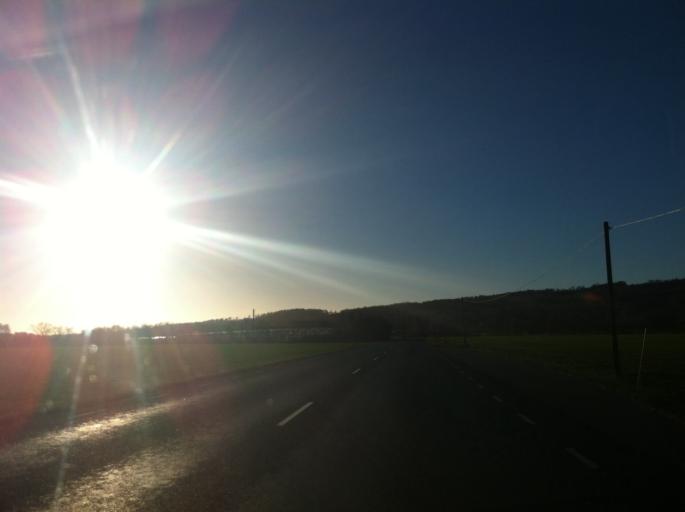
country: SE
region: Skane
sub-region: Bromolla Kommun
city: Nasum
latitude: 56.1857
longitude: 14.5105
